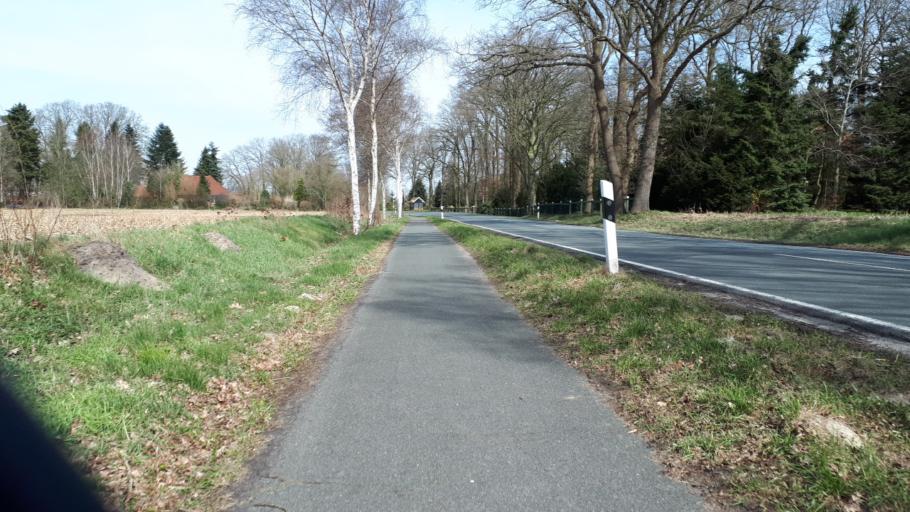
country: DE
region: Lower Saxony
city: Wardenburg
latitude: 53.0504
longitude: 8.1782
